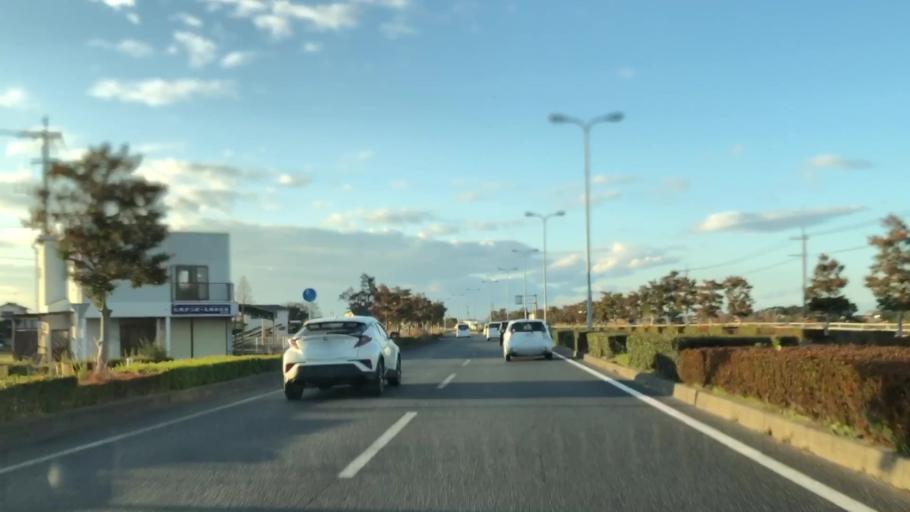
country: JP
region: Fukuoka
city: Nakatsu
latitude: 33.5434
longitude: 131.2874
